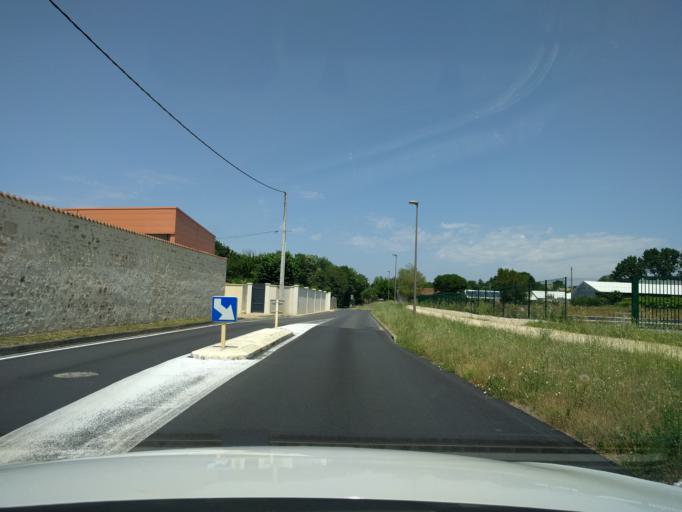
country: FR
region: Poitou-Charentes
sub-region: Departement des Deux-Sevres
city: Niort
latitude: 46.3384
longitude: -0.4642
